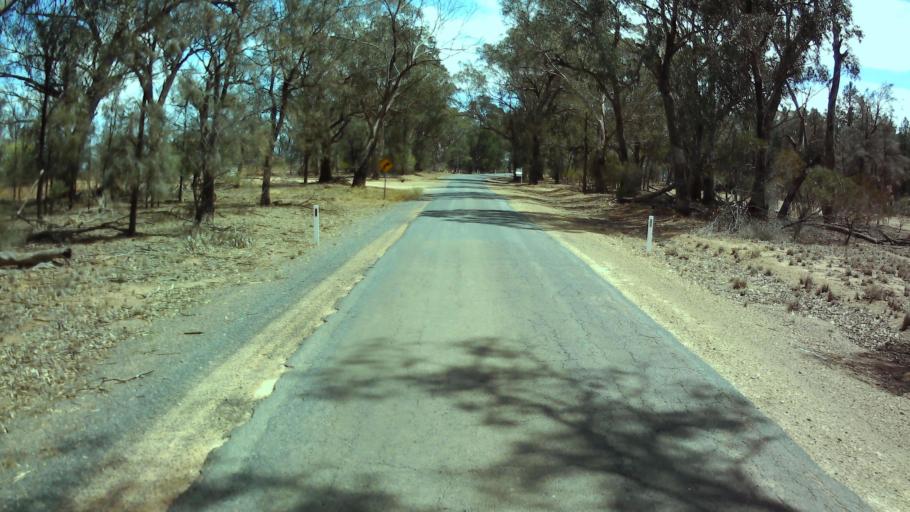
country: AU
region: New South Wales
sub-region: Weddin
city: Grenfell
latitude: -33.6447
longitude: 148.1909
